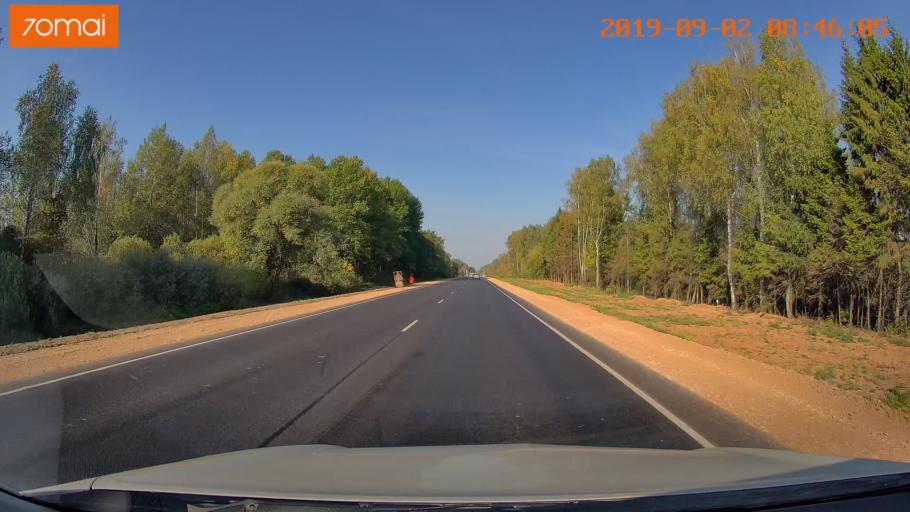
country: RU
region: Kaluga
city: Medyn'
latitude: 54.9690
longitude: 35.9873
